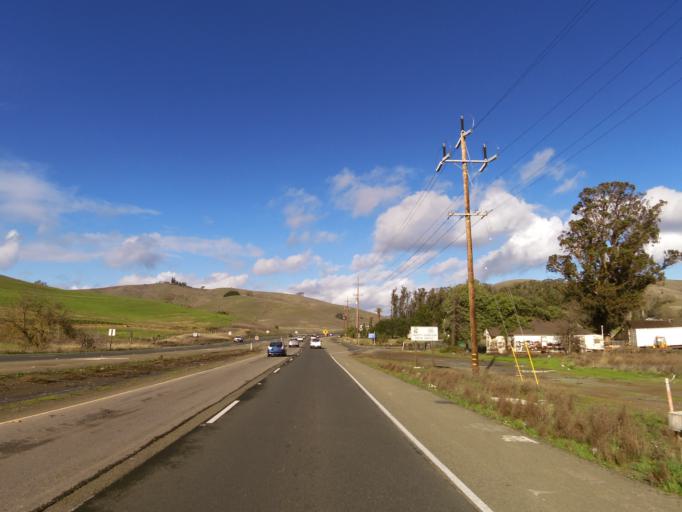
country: US
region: California
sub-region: Sonoma County
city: Petaluma
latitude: 38.1870
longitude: -122.6008
